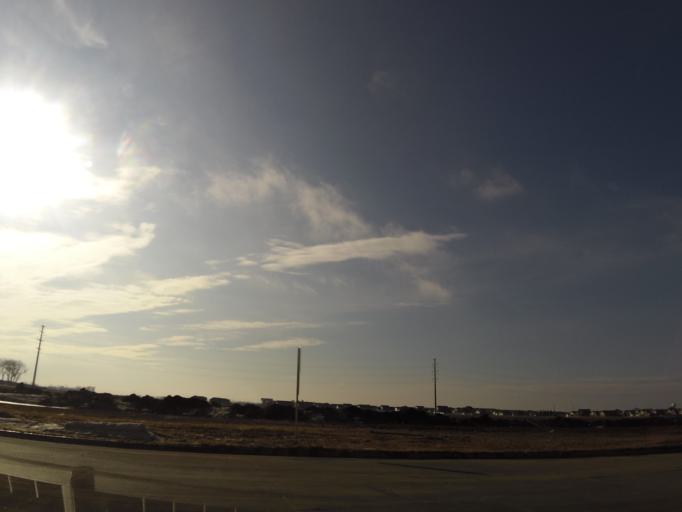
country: US
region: North Dakota
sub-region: Grand Forks County
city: Grand Forks
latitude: 47.8787
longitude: -97.0641
